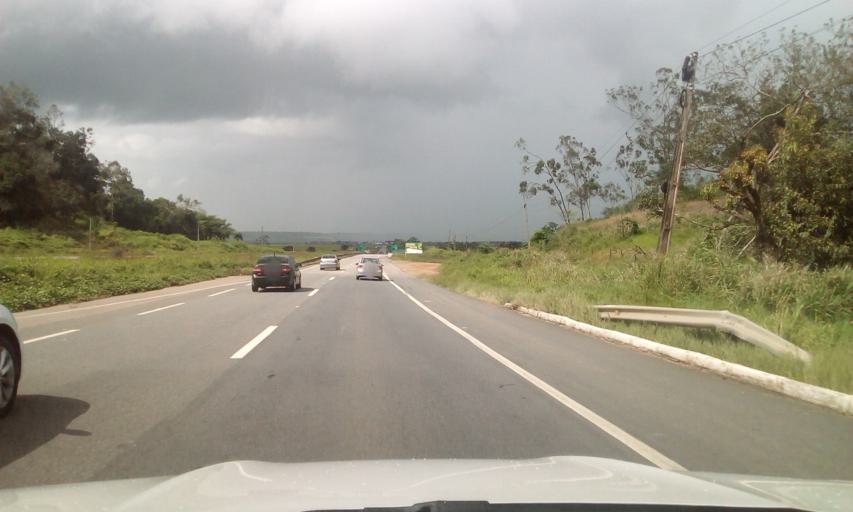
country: BR
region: Pernambuco
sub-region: Goiana
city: Goiana
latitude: -7.5327
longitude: -34.9915
